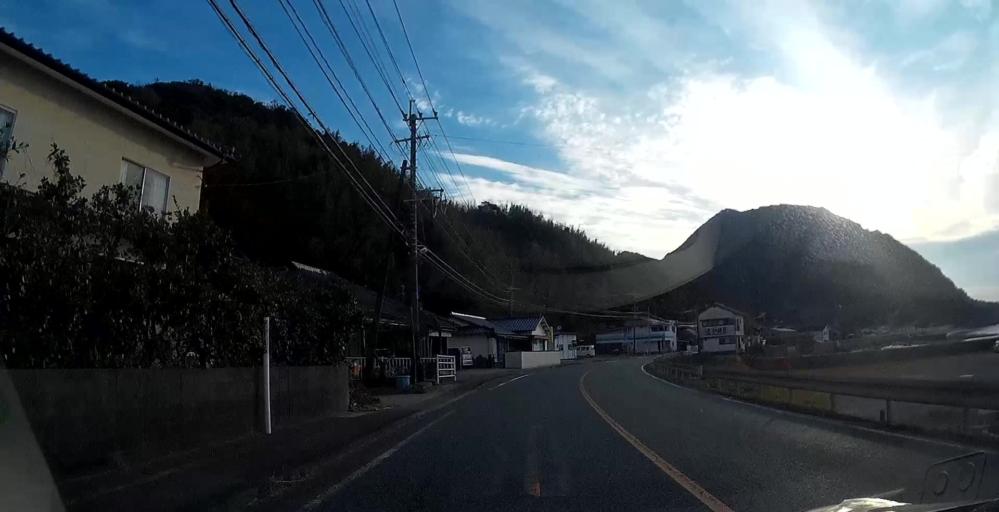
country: JP
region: Nagasaki
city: Shimabara
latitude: 32.6399
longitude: 130.4784
